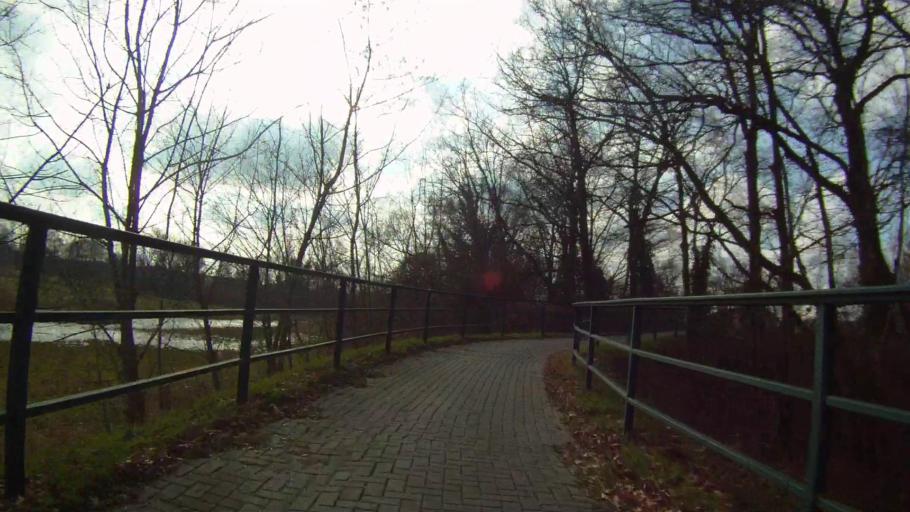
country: DE
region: Brandenburg
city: Erkner
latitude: 52.3930
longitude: 13.7454
